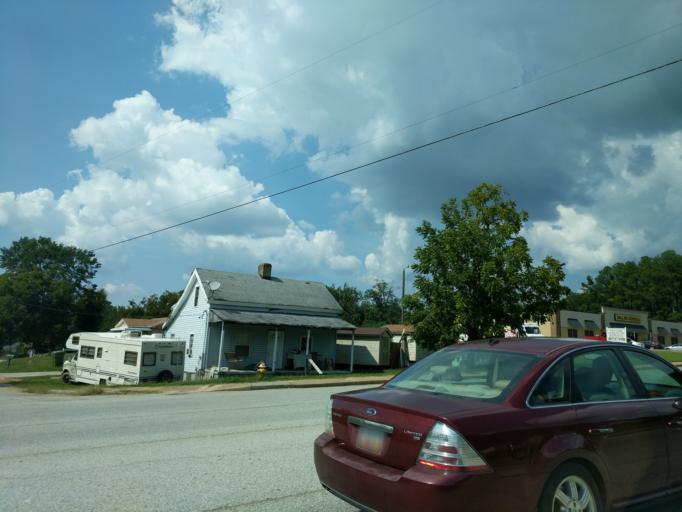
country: US
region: South Carolina
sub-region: Greenville County
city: Five Forks
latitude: 34.8598
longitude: -82.2238
